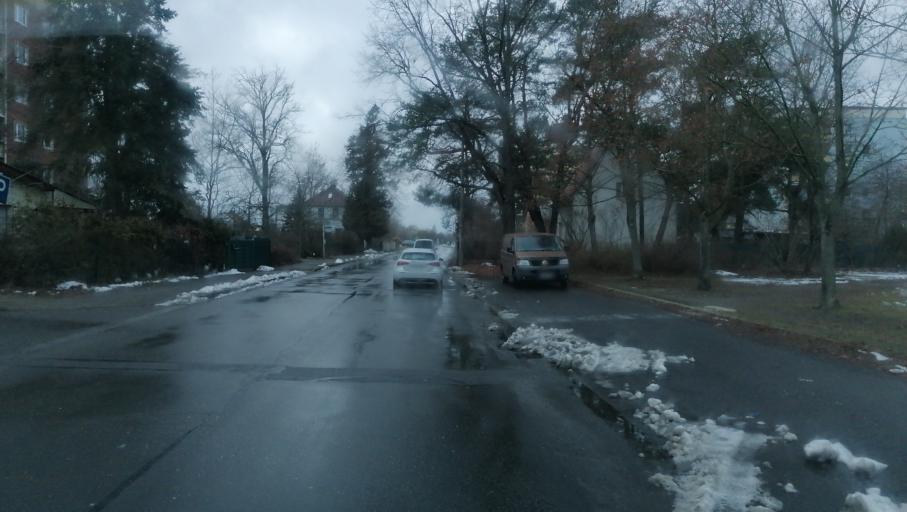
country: DE
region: Brandenburg
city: Cottbus
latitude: 51.7211
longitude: 14.3362
